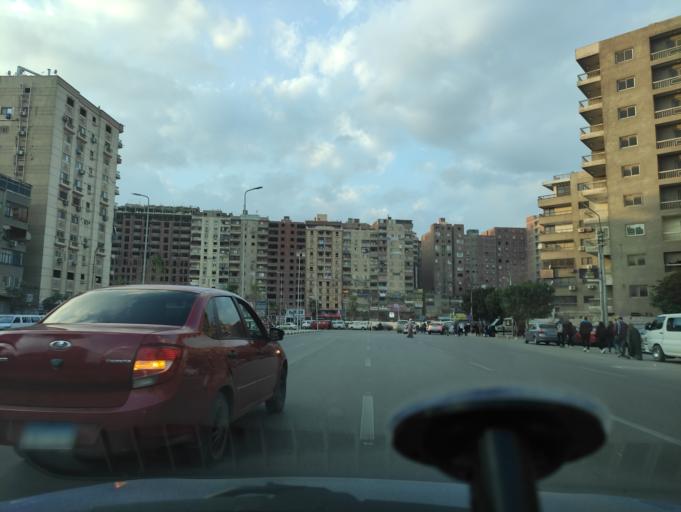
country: EG
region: Muhafazat al Qalyubiyah
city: Al Khankah
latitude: 30.1179
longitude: 31.3412
